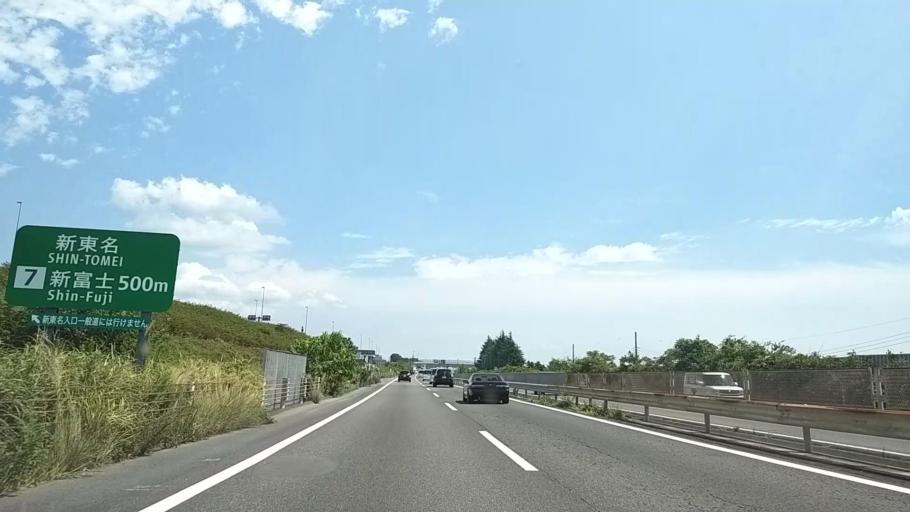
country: JP
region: Shizuoka
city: Fuji
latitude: 35.2016
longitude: 138.6599
